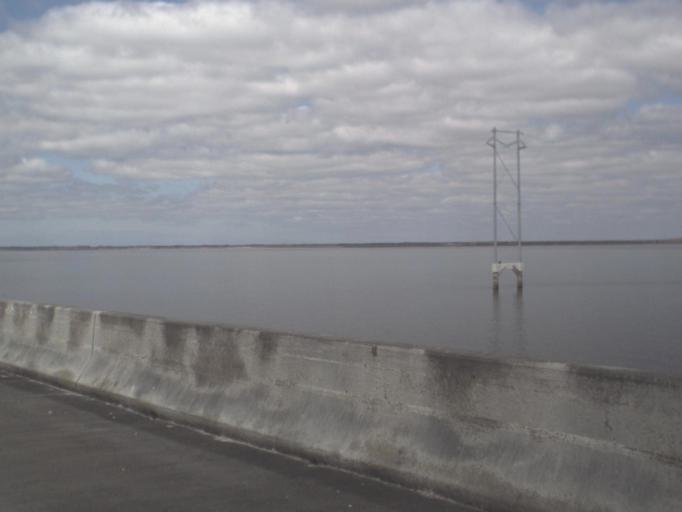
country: US
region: Florida
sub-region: Franklin County
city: Eastpoint
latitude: 29.7324
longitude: -84.9228
